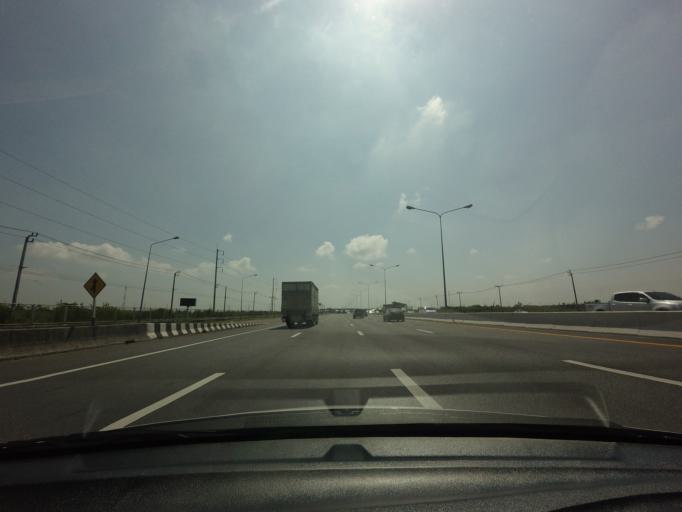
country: TH
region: Samut Prakan
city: Ban Khlong Bang Sao Thong
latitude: 13.6530
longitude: 100.8704
